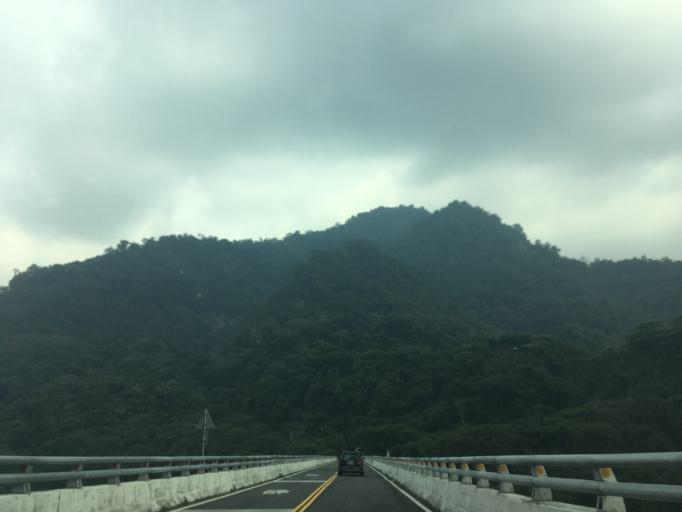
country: TW
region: Taiwan
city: Fengyuan
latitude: 24.2947
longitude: 120.9101
